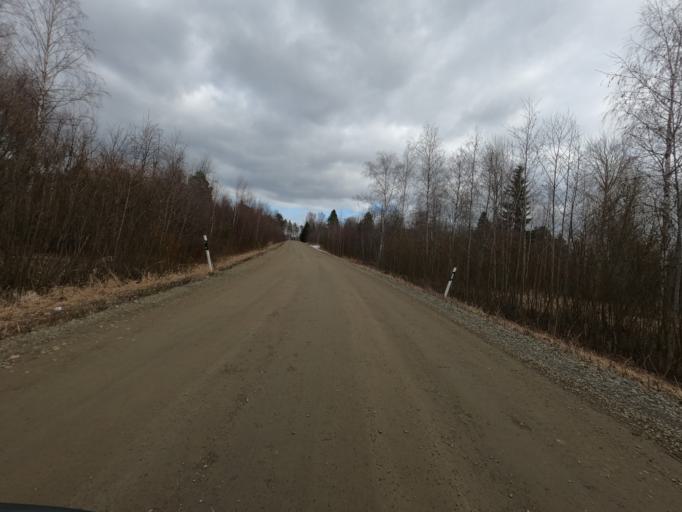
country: FI
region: North Karelia
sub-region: Joensuu
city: Joensuu
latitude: 62.5671
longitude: 29.8026
